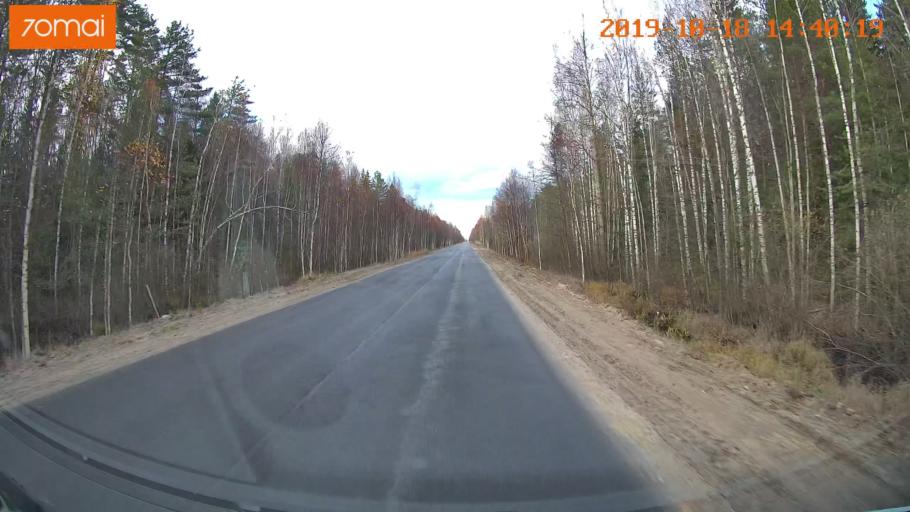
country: RU
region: Vladimir
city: Velikodvorskiy
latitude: 55.2747
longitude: 40.6688
